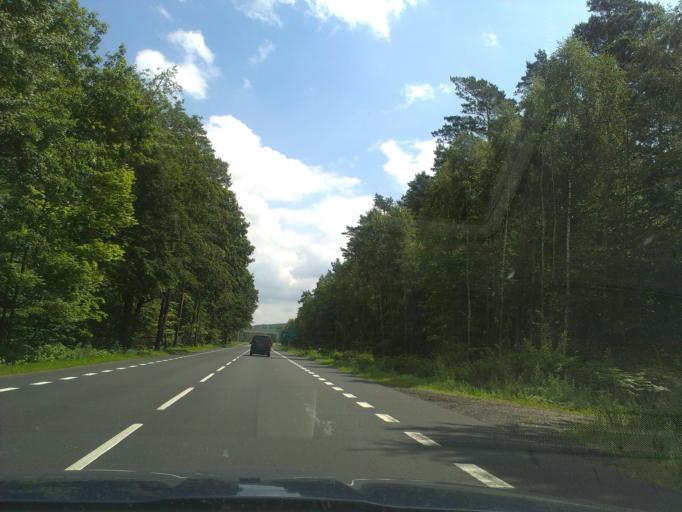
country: PL
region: West Pomeranian Voivodeship
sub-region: Powiat kamienski
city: Miedzyzdroje
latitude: 53.9150
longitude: 14.4149
